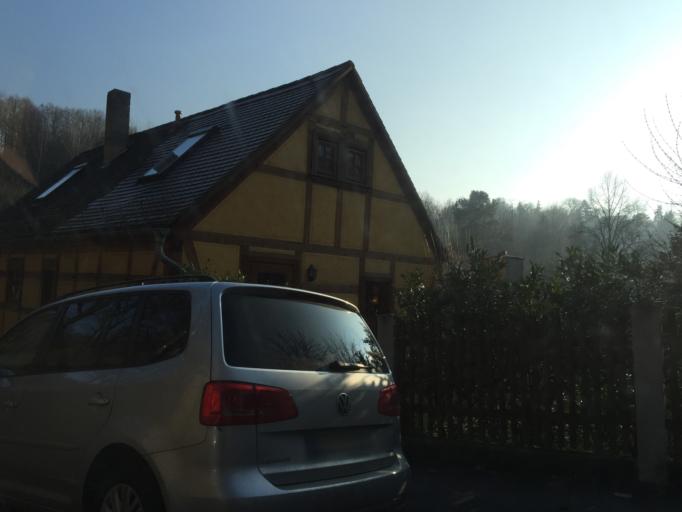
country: DE
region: Saxony
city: Albertstadt
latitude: 51.0591
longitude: 13.8282
